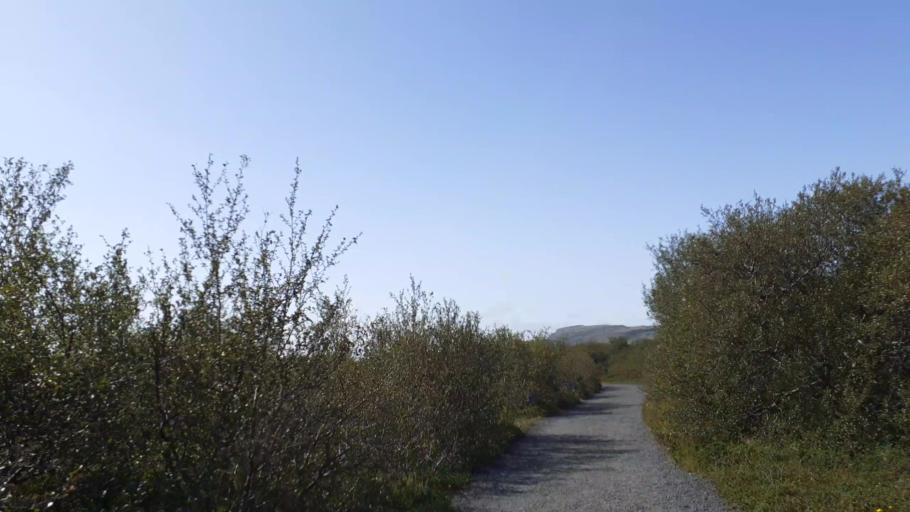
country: IS
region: West
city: Borgarnes
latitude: 64.7534
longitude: -21.5502
